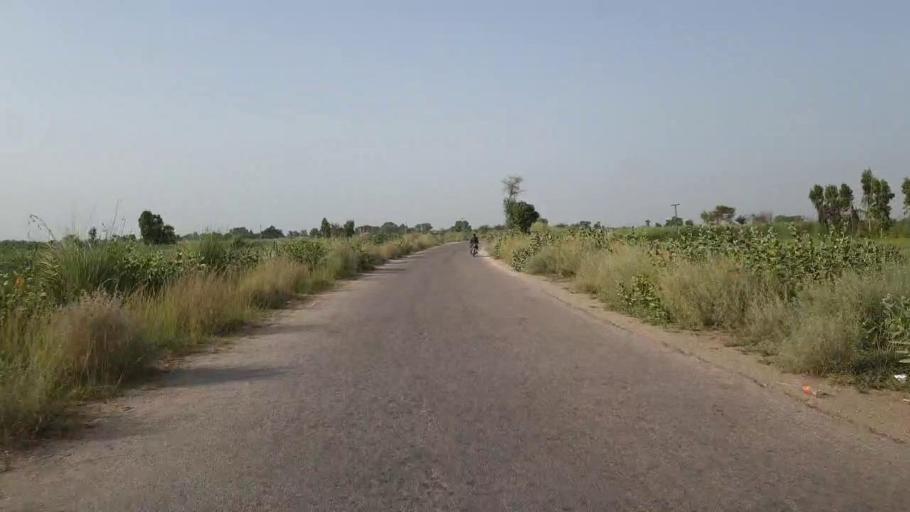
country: PK
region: Sindh
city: Jam Sahib
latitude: 26.4208
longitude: 68.8705
